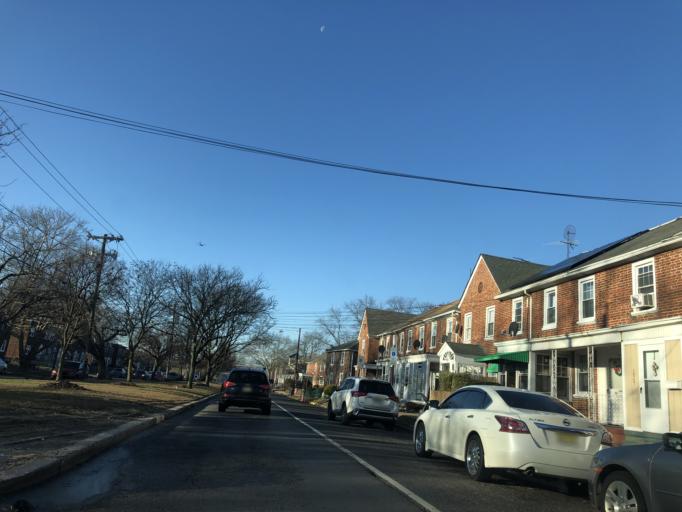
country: US
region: New Jersey
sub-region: Camden County
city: Gloucester City
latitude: 39.9033
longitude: -75.1074
